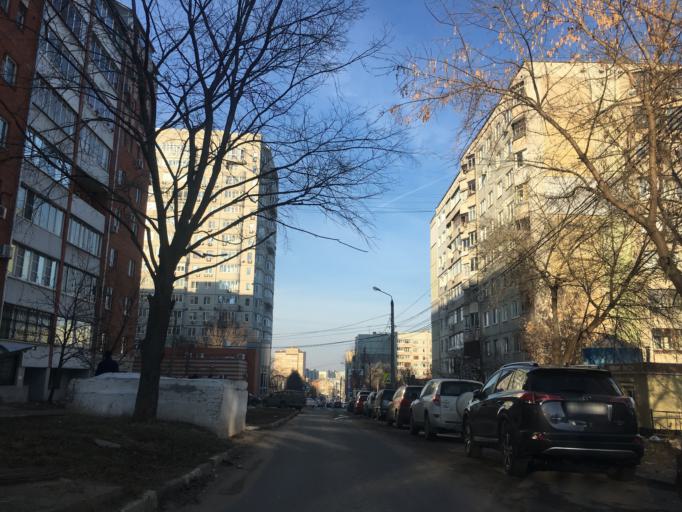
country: RU
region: Tula
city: Tula
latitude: 54.1931
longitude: 37.5884
